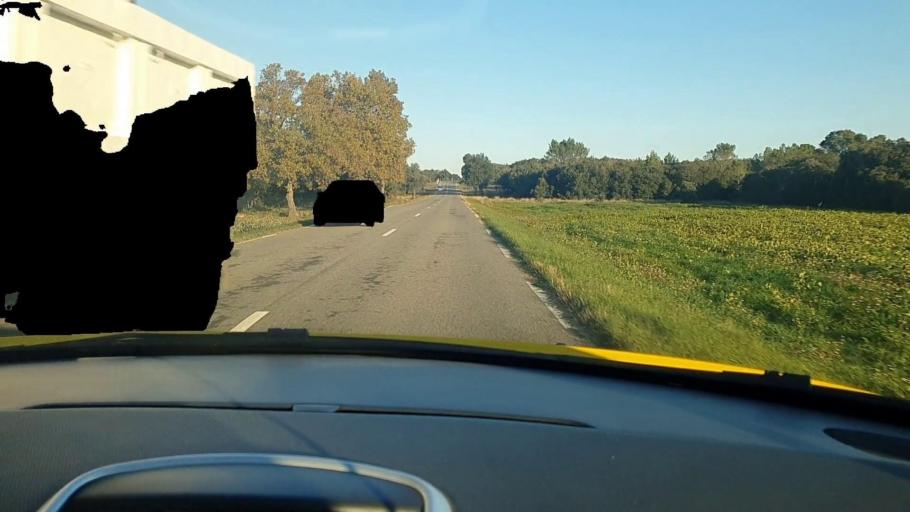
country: FR
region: Languedoc-Roussillon
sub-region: Departement du Gard
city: Montaren-et-Saint-Mediers
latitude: 44.0879
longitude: 4.3899
